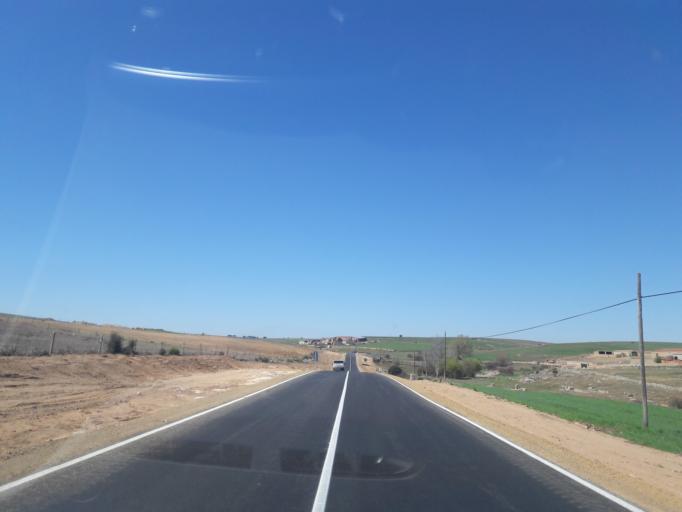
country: ES
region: Castille and Leon
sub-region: Provincia de Salamanca
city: Valdemierque
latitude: 40.8243
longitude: -5.5717
